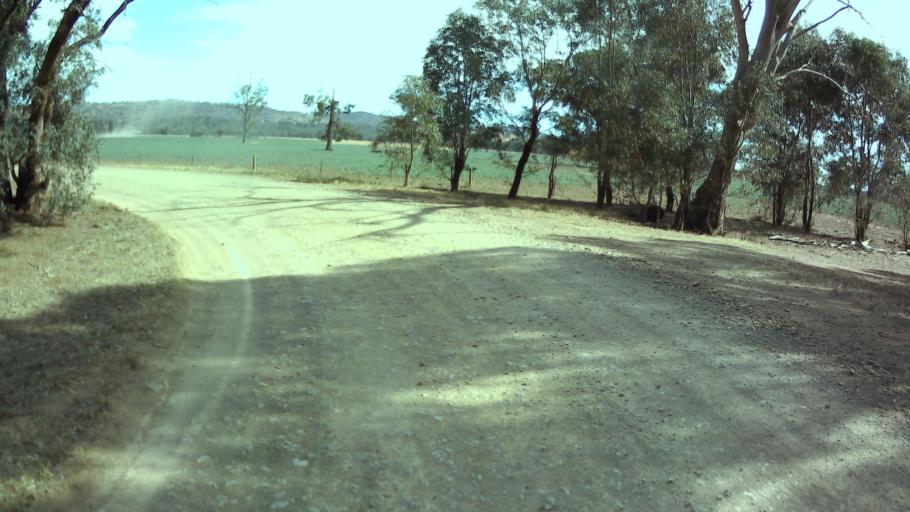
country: AU
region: New South Wales
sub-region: Weddin
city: Grenfell
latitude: -33.6872
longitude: 148.3053
